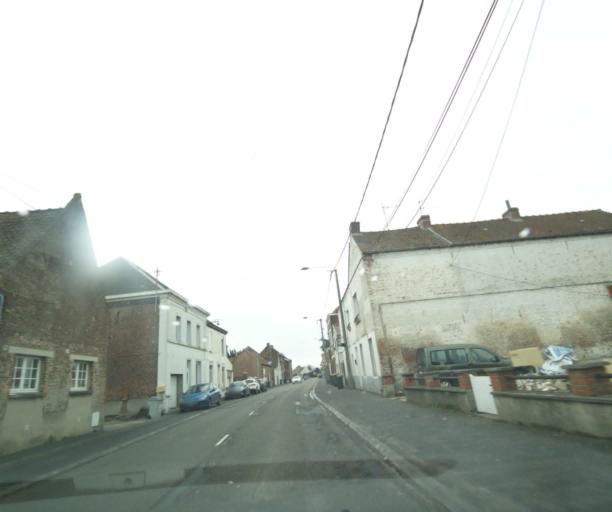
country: FR
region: Nord-Pas-de-Calais
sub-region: Departement du Nord
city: Crespin
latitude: 50.4197
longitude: 3.6611
